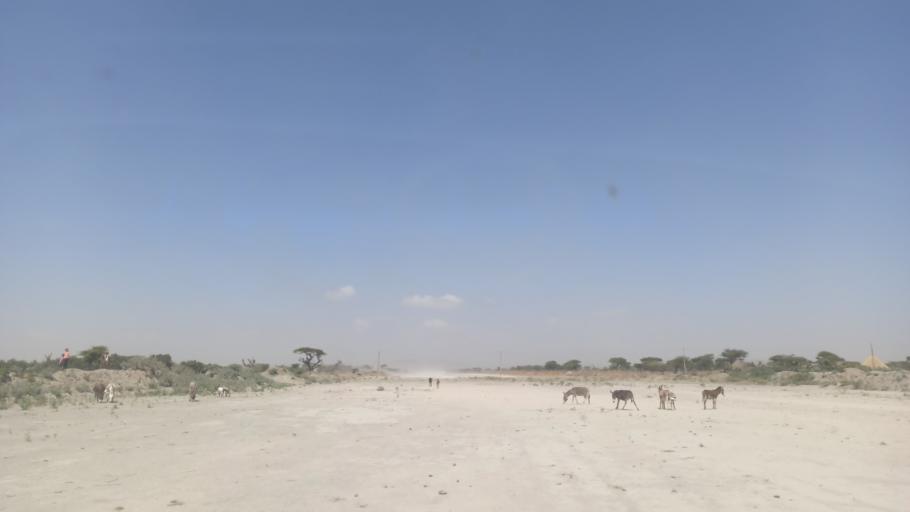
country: ET
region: Oromiya
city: Ziway
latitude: 7.7110
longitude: 38.6358
